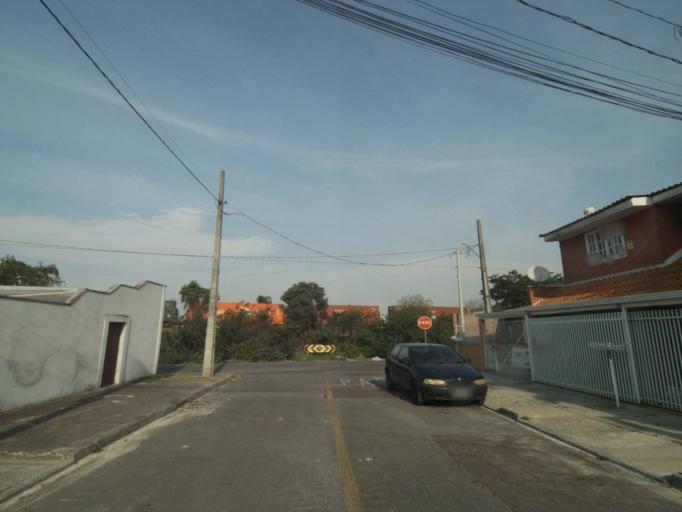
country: BR
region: Parana
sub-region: Pinhais
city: Pinhais
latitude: -25.4856
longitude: -49.2010
